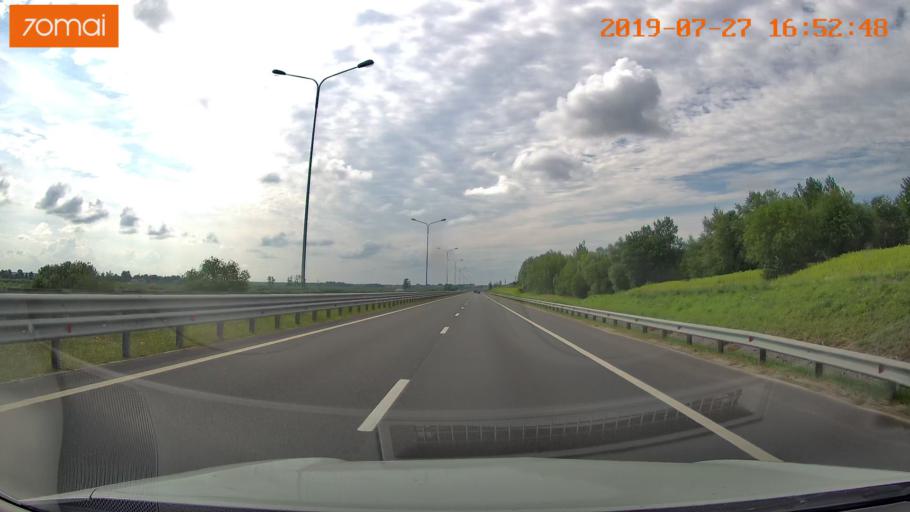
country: RU
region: Kaliningrad
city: Gvardeysk
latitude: 54.6846
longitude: 20.8481
